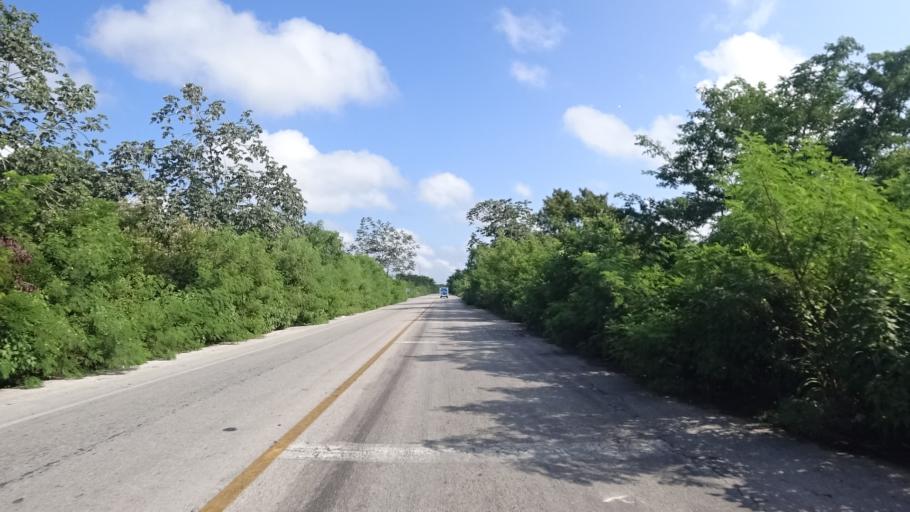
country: MX
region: Yucatan
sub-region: Valladolid
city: Dzitnup
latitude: 20.6910
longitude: -88.2448
